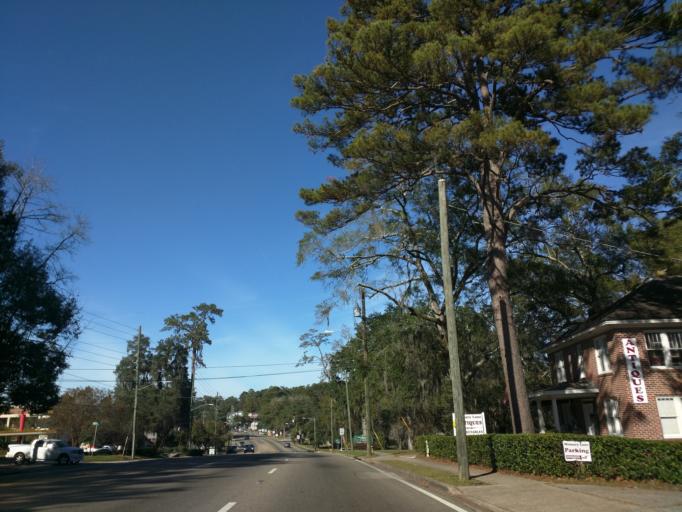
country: US
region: Florida
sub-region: Leon County
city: Tallahassee
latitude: 30.4588
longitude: -84.2808
